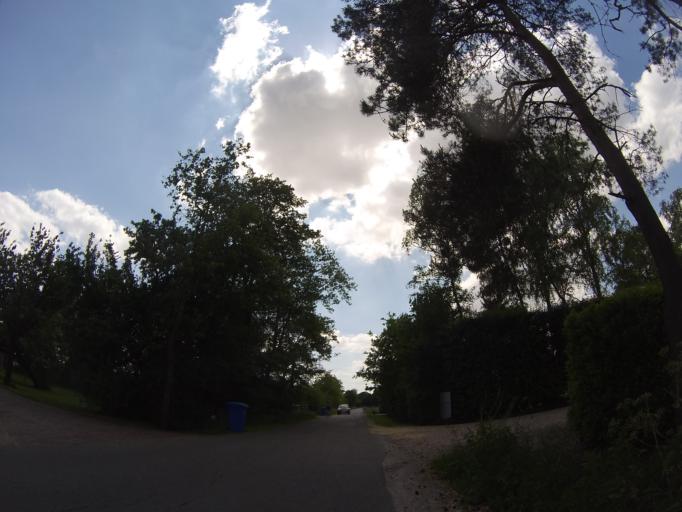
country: NL
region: Gelderland
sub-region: Gemeente Barneveld
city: Stroe
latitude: 52.1904
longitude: 5.6499
